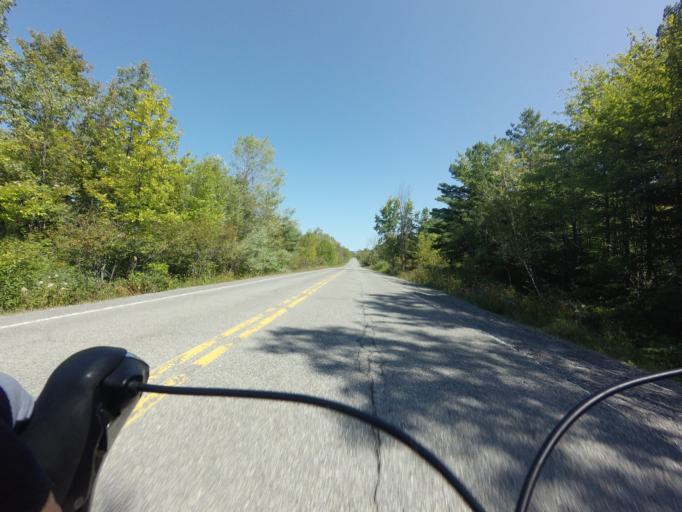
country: CA
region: Ontario
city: Bells Corners
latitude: 45.3911
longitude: -76.0673
